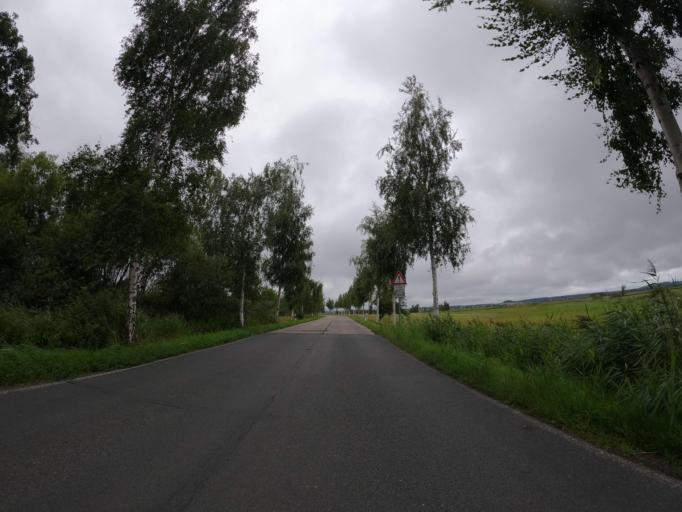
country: DE
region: Mecklenburg-Vorpommern
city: Ostseebad Gohren
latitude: 54.3062
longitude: 13.6973
